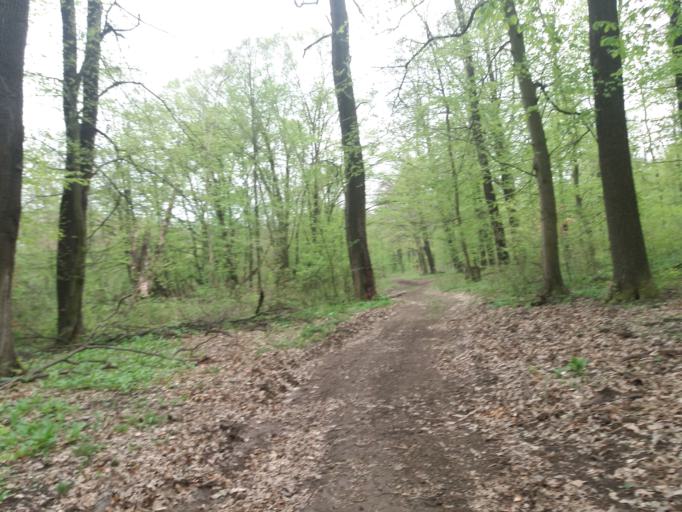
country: HU
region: Komarom-Esztergom
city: Labatlan
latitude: 47.6859
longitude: 18.5137
